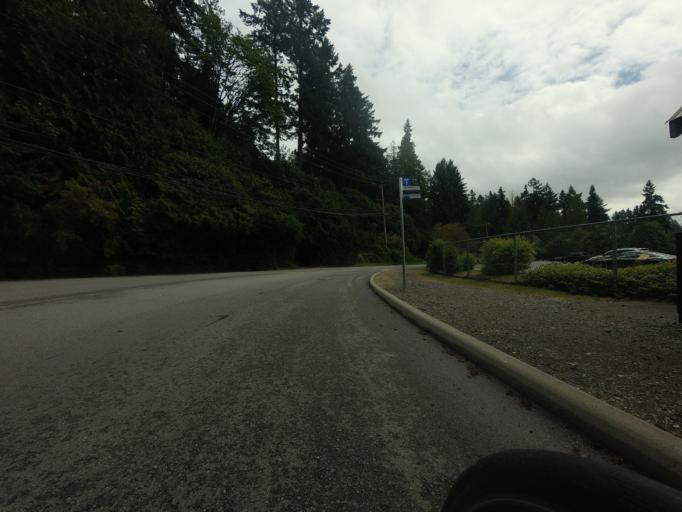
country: CA
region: British Columbia
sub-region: Greater Vancouver Regional District
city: Bowen Island
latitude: 49.3586
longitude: -123.2671
